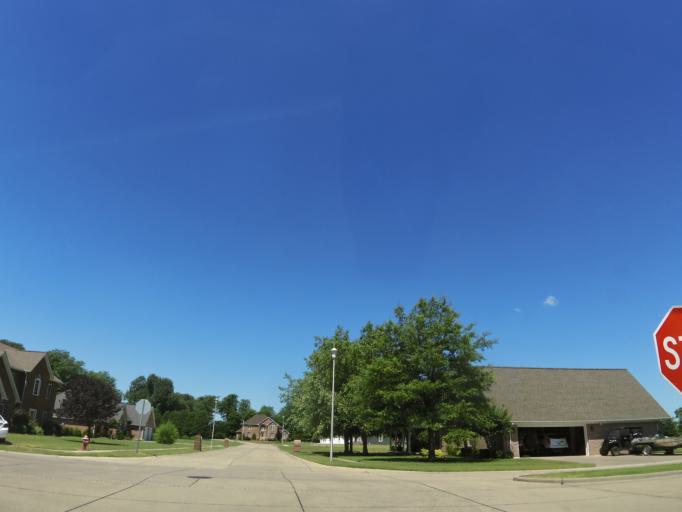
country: US
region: Missouri
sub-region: New Madrid County
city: New Madrid
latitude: 36.5996
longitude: -89.5265
